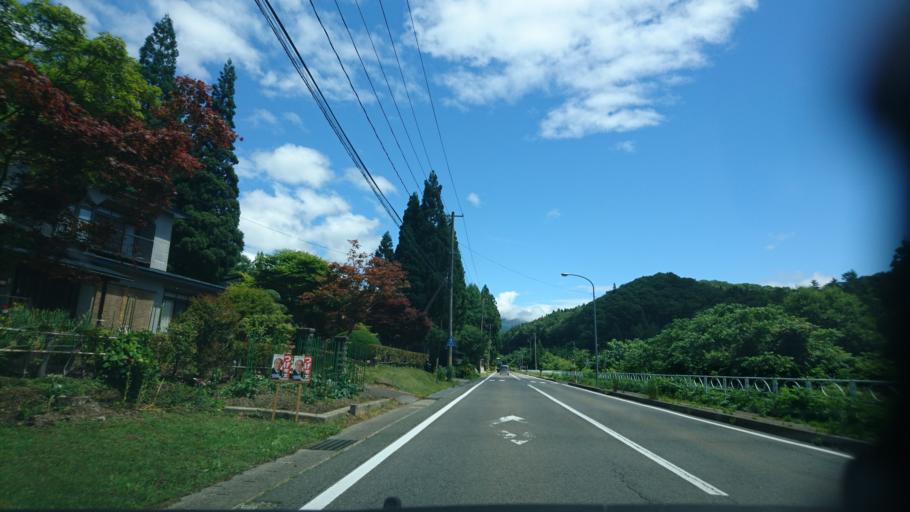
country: JP
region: Akita
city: Kakunodatemachi
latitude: 39.6720
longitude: 140.6949
